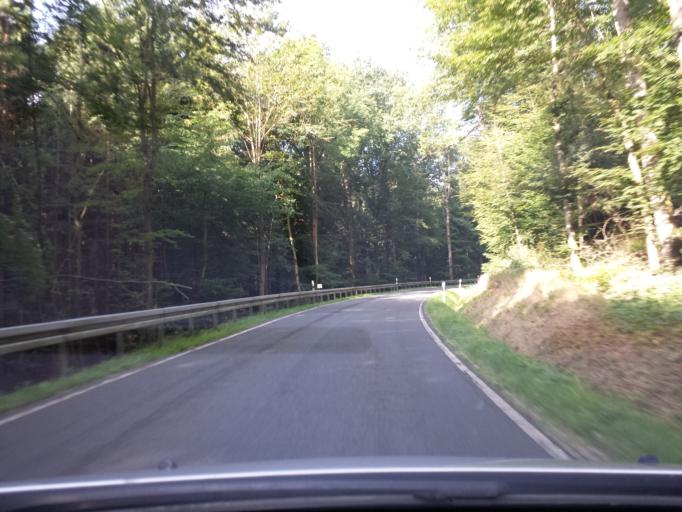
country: DE
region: Hesse
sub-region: Regierungsbezirk Kassel
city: Bad Hersfeld
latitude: 50.8696
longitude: 9.6612
